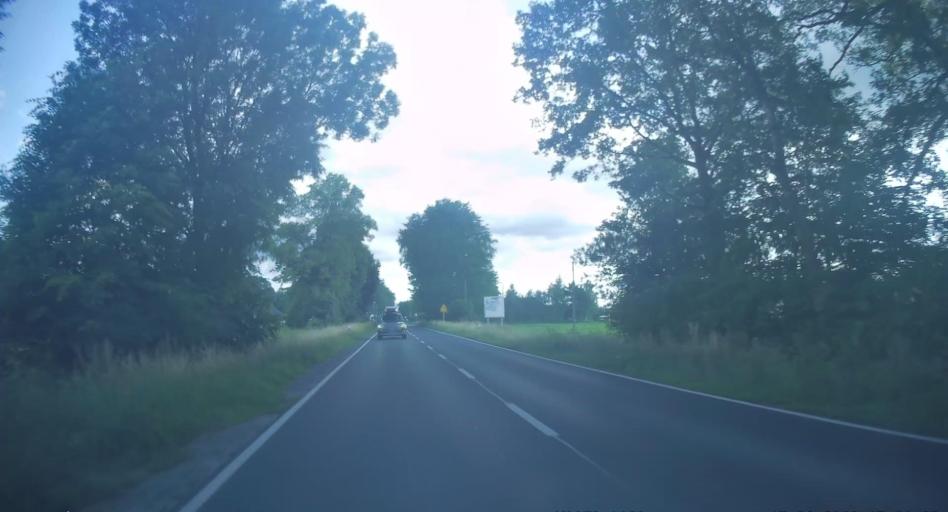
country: PL
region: Lesser Poland Voivodeship
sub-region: Powiat oswiecimski
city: Grojec
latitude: 49.9567
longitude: 19.2131
